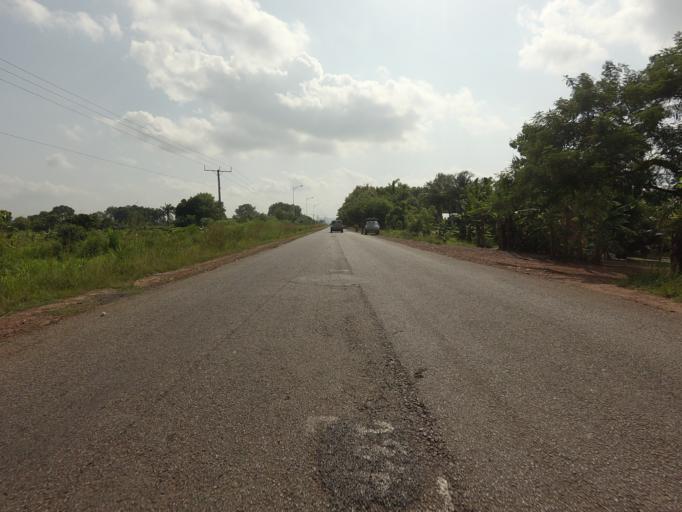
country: GH
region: Volta
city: Ho
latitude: 6.5966
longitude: 0.5248
